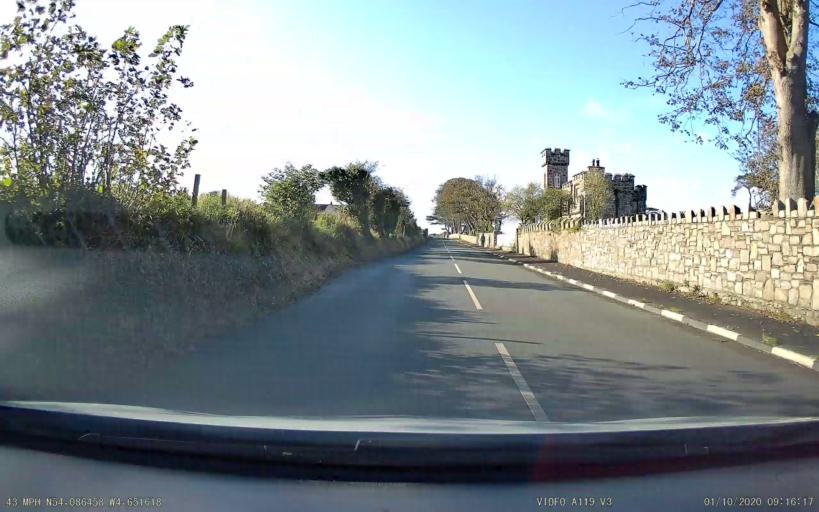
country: IM
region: Castletown
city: Castletown
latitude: 54.0865
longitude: -4.6516
